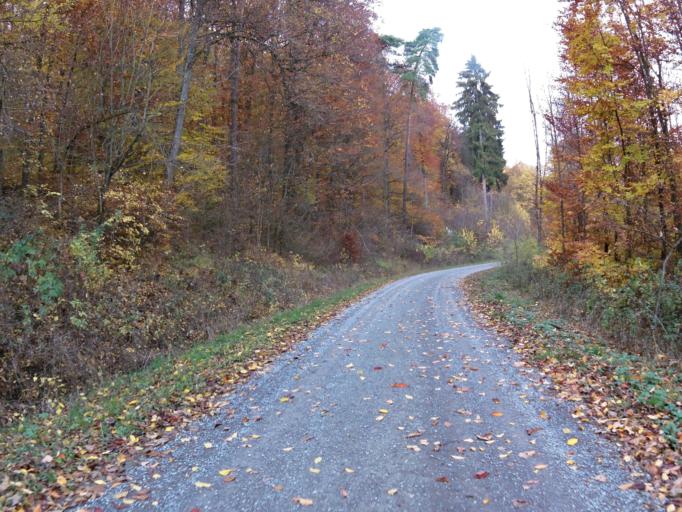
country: DE
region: Bavaria
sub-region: Regierungsbezirk Unterfranken
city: Waldbrunn
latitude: 49.7496
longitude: 9.8109
